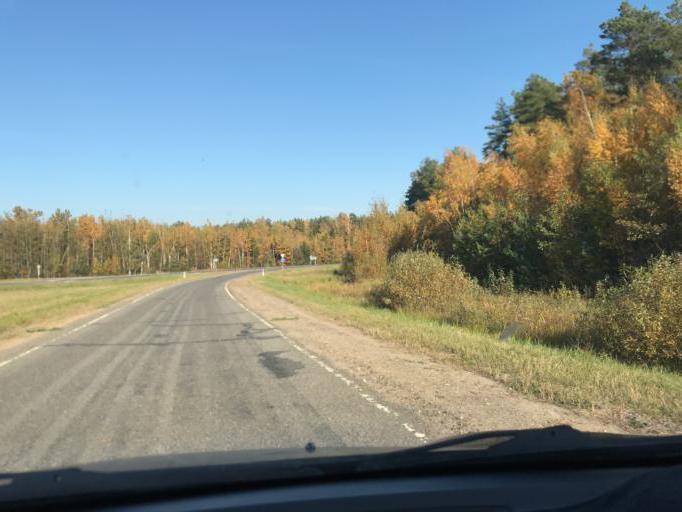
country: BY
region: Mogilev
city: Babruysk
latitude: 53.1052
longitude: 29.0592
